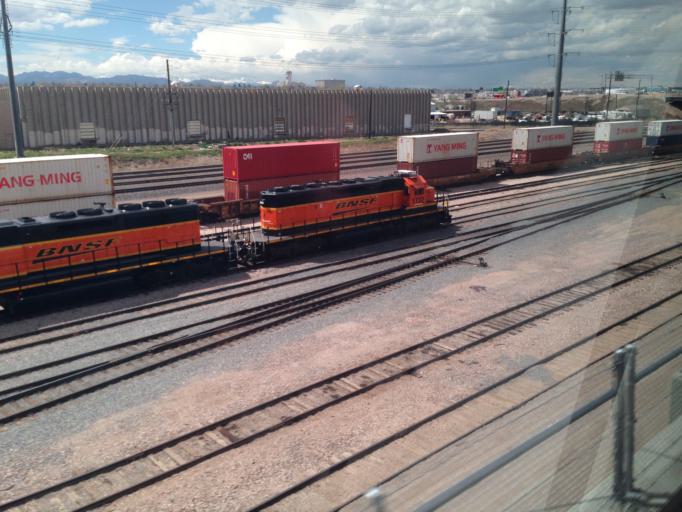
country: US
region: Colorado
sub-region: Adams County
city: Berkley
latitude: 39.7807
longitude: -104.9971
